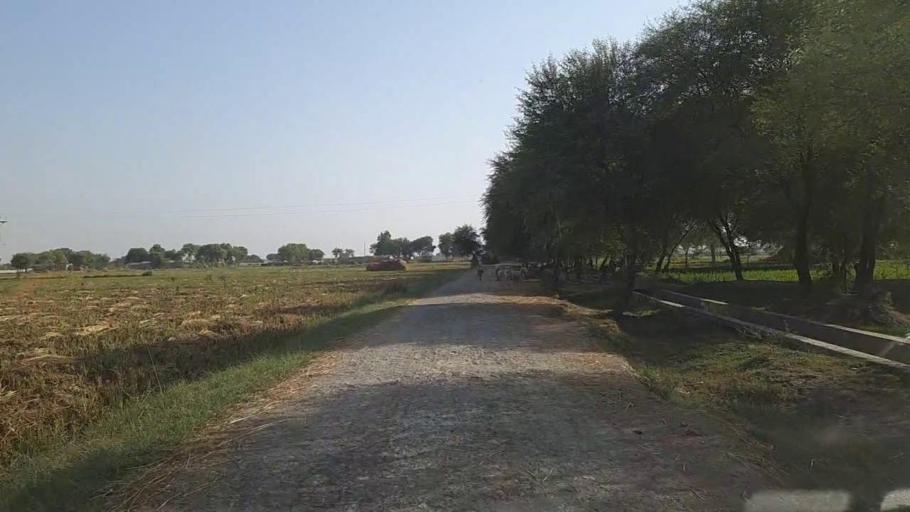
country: PK
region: Sindh
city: Kandhkot
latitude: 28.3537
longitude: 69.3351
